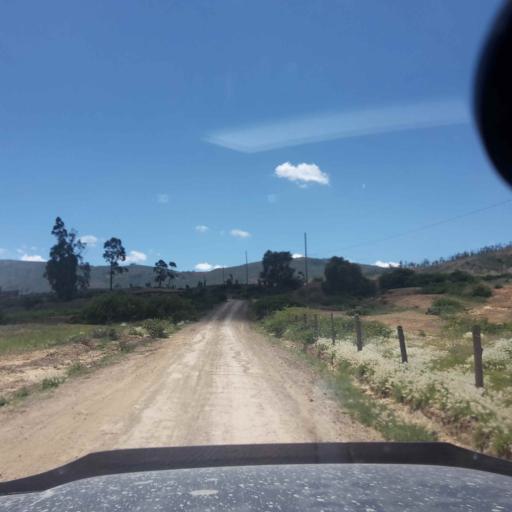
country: BO
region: Cochabamba
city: Totora
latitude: -17.7738
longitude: -65.2462
